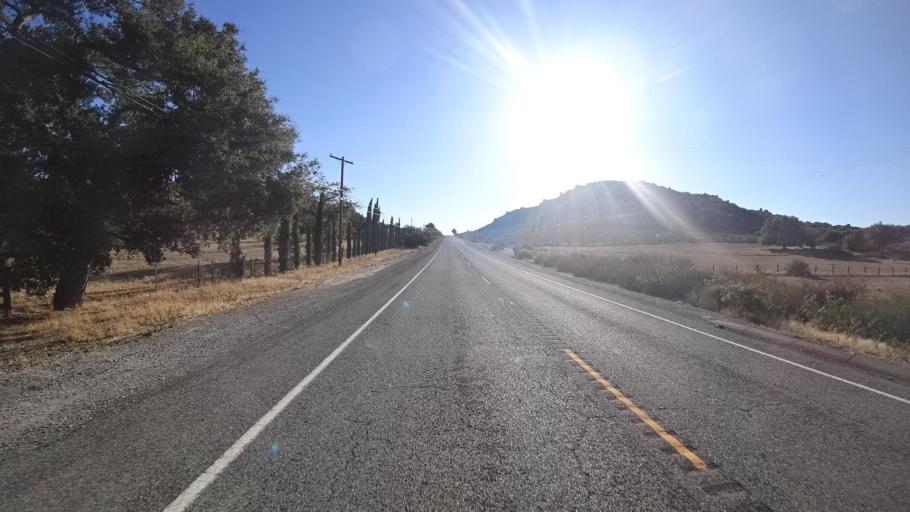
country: MX
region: Baja California
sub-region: Tecate
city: Hacienda Tecate
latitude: 32.5973
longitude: -116.5558
